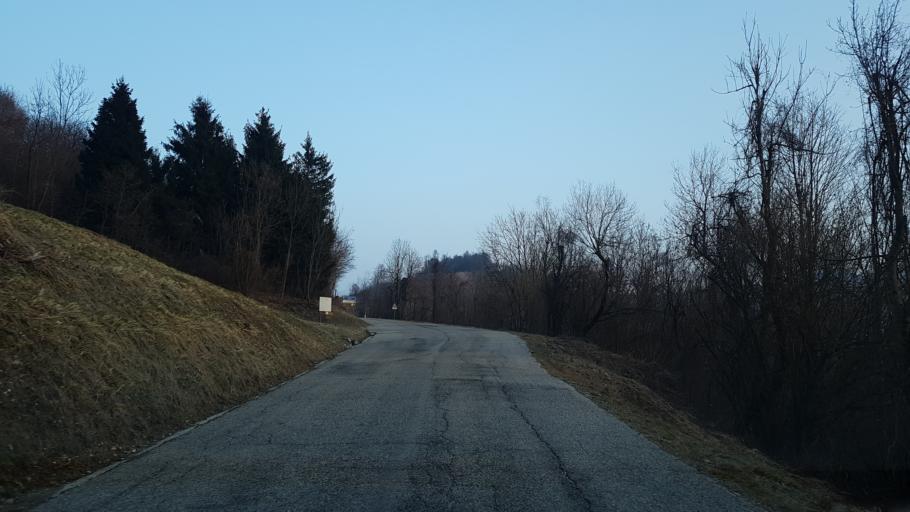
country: IT
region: Friuli Venezia Giulia
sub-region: Provincia di Udine
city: Taipana
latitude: 46.2602
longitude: 13.3479
